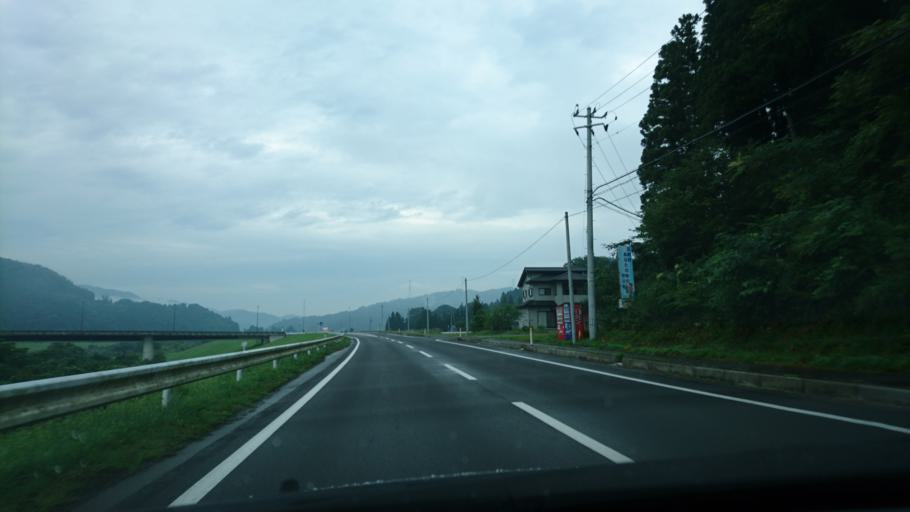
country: JP
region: Iwate
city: Ichinoseki
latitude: 38.9161
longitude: 141.2572
